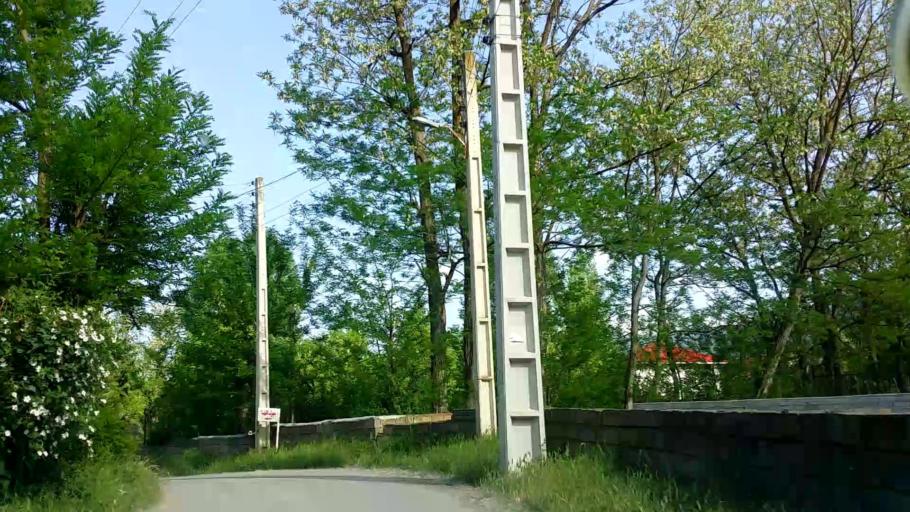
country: IR
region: Mazandaran
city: `Abbasabad
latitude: 36.5228
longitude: 51.1748
